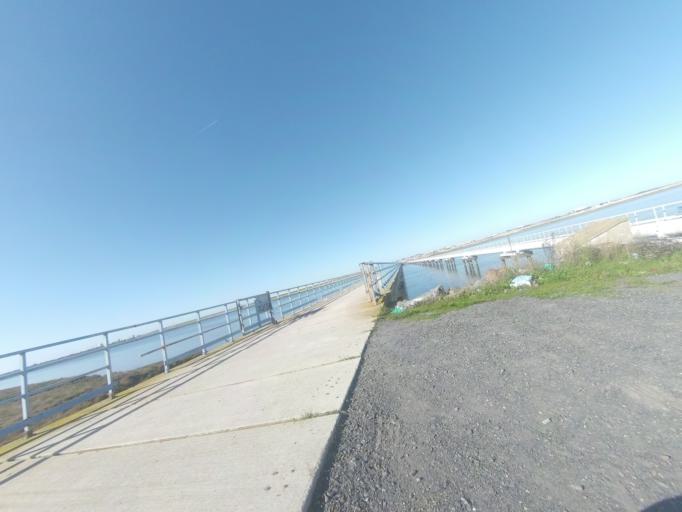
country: ES
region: Andalusia
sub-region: Provincia de Huelva
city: Palos de la Frontera
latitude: 37.2465
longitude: -6.8936
